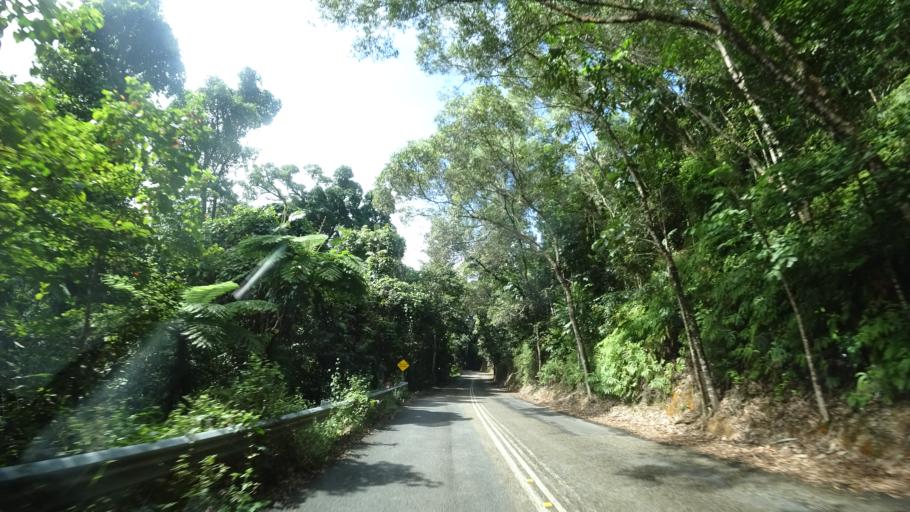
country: AU
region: Queensland
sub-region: Cairns
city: Port Douglas
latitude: -16.2515
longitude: 145.4325
